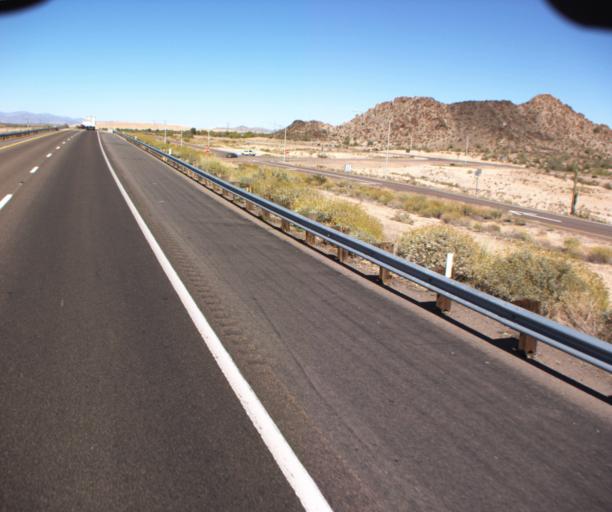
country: US
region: Arizona
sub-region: Maricopa County
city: Buckeye
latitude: 33.1948
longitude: -112.6506
